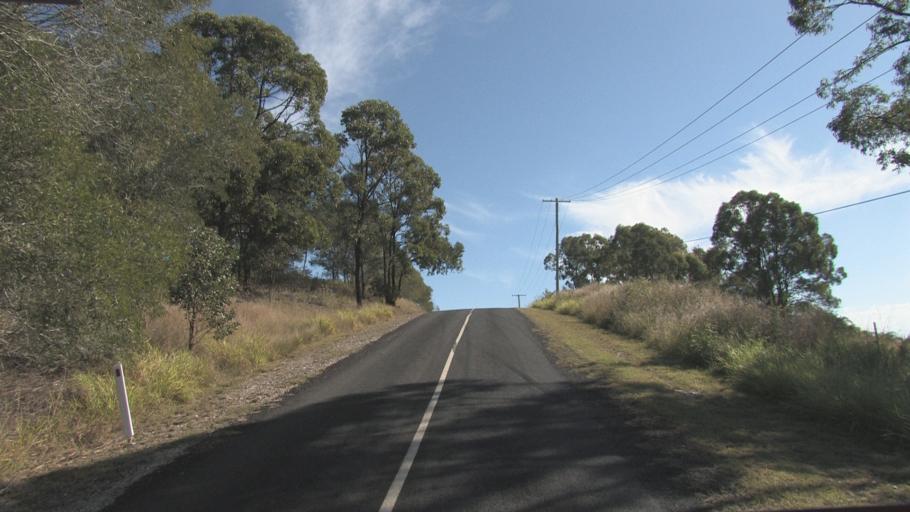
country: AU
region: Queensland
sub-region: Logan
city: Windaroo
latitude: -27.7420
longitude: 153.1742
